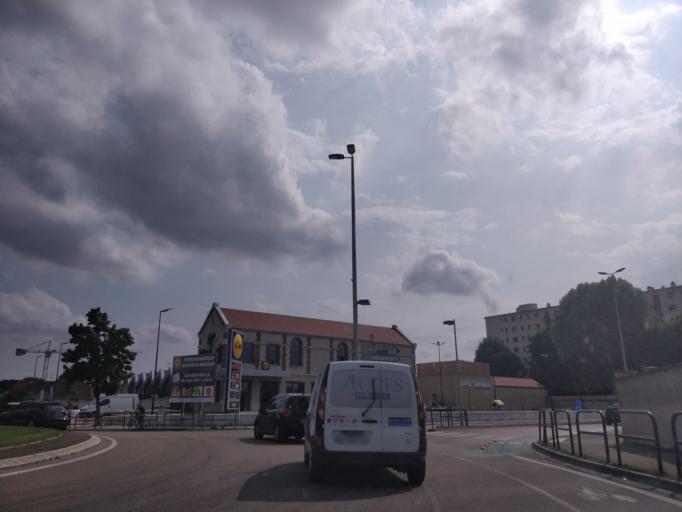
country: FR
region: Champagne-Ardenne
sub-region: Departement de l'Aube
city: Troyes
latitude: 48.2880
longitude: 4.0808
